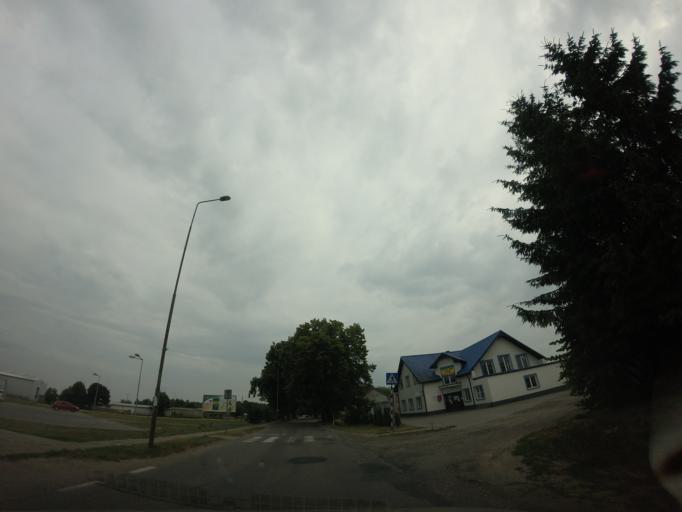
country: PL
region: West Pomeranian Voivodeship
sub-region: Powiat drawski
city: Czaplinek
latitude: 53.5518
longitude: 16.2325
